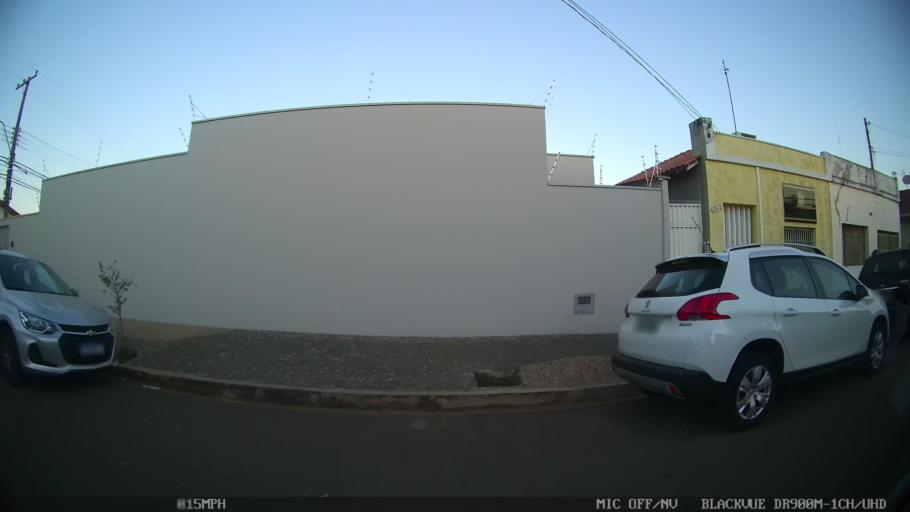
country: BR
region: Sao Paulo
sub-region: Santa Barbara D'Oeste
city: Santa Barbara d'Oeste
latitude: -22.7584
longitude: -47.4140
